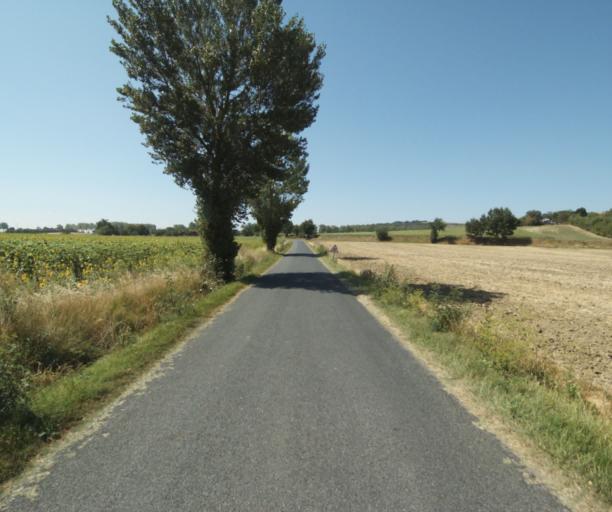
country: FR
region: Midi-Pyrenees
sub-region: Departement de la Haute-Garonne
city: Revel
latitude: 43.5106
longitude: 1.9528
